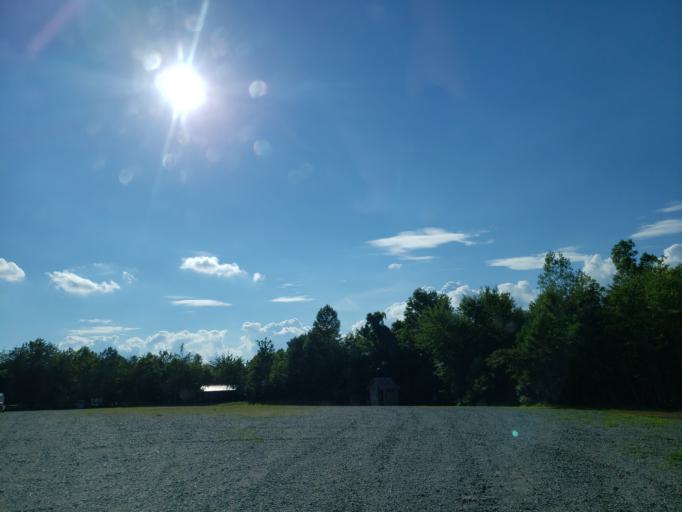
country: US
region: Georgia
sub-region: Bartow County
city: Rydal
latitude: 34.3658
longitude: -84.6203
